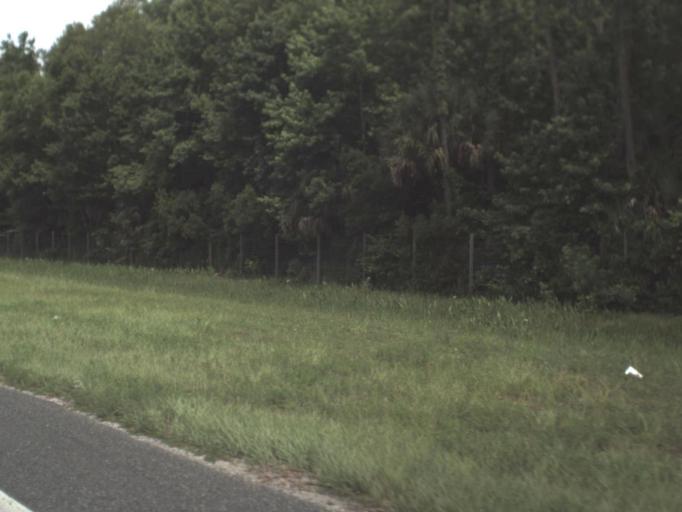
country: US
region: Florida
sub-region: Putnam County
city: Palatka
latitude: 29.6300
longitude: -81.7525
